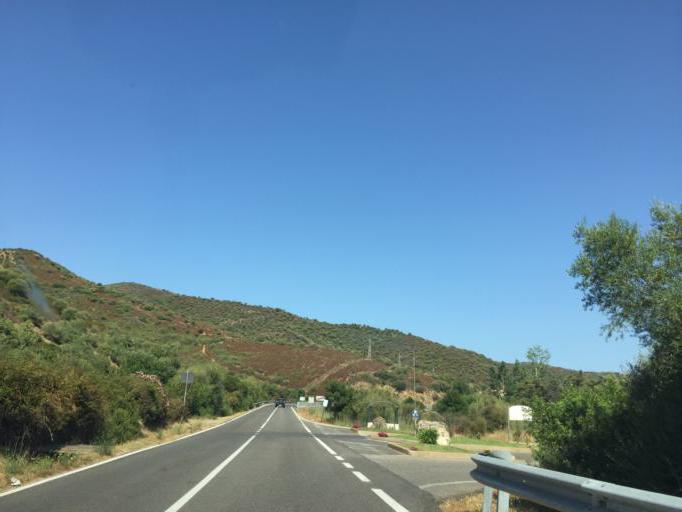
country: IT
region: Sardinia
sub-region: Provincia di Olbia-Tempio
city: San Teodoro
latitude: 40.7306
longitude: 9.6509
